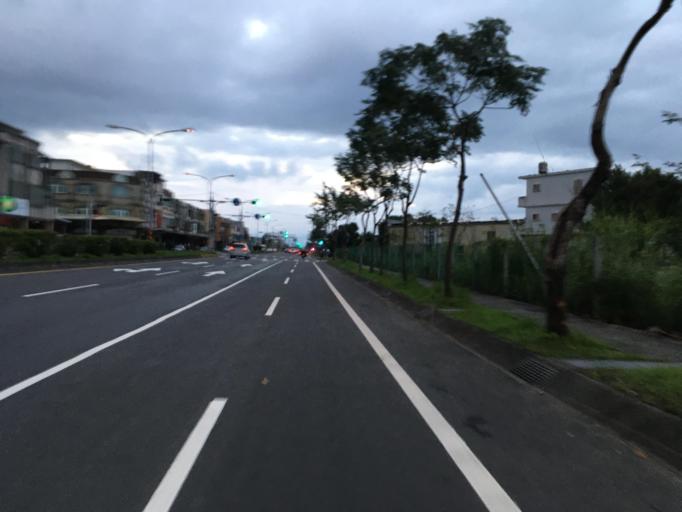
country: TW
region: Taiwan
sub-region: Yilan
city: Yilan
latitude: 24.6210
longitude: 121.8414
